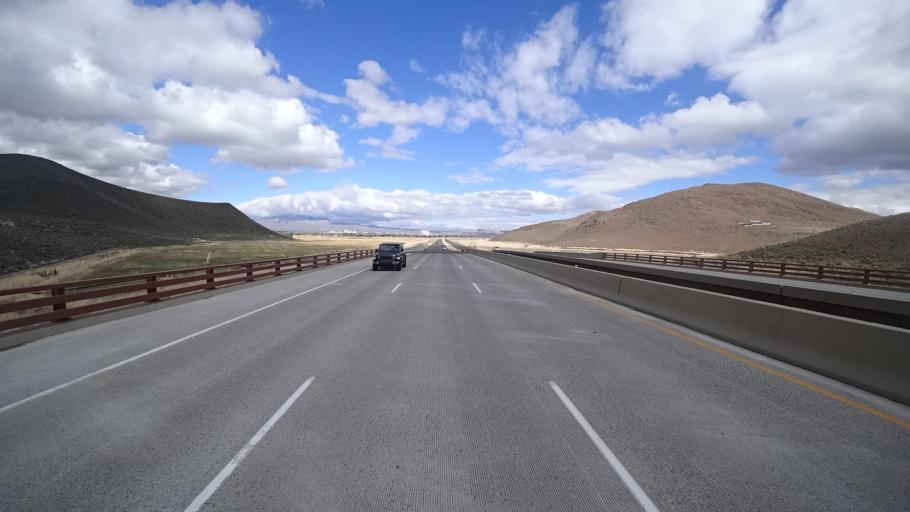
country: US
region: Nevada
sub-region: Washoe County
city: Sparks
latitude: 39.4667
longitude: -119.7302
